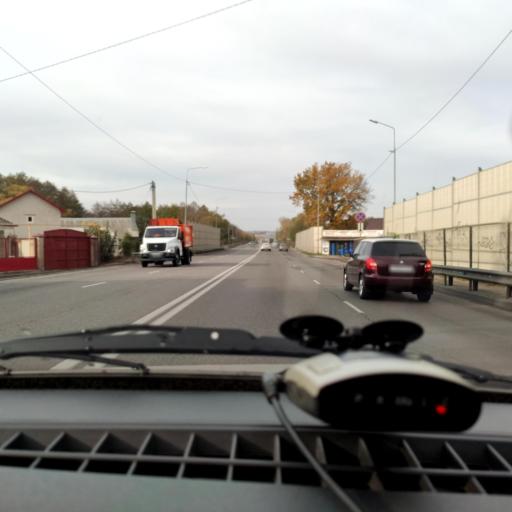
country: RU
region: Voronezj
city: Pridonskoy
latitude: 51.6491
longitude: 39.0905
